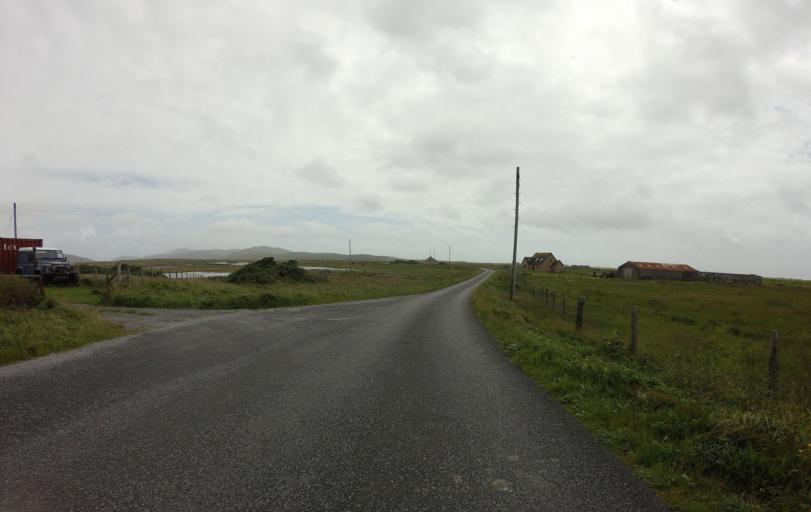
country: GB
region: Scotland
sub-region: Eilean Siar
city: Isle of South Uist
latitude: 57.2585
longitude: -7.4052
